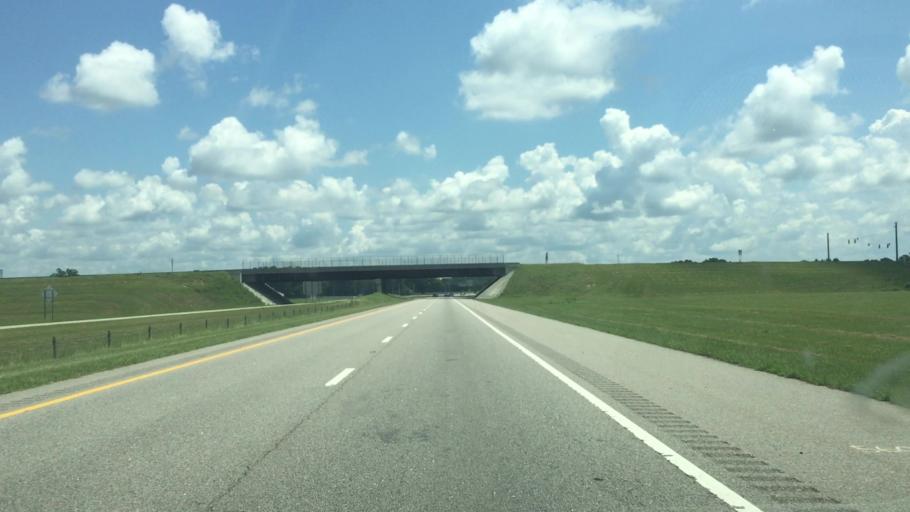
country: US
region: North Carolina
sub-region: Robeson County
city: Lumberton
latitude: 34.5923
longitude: -79.0913
